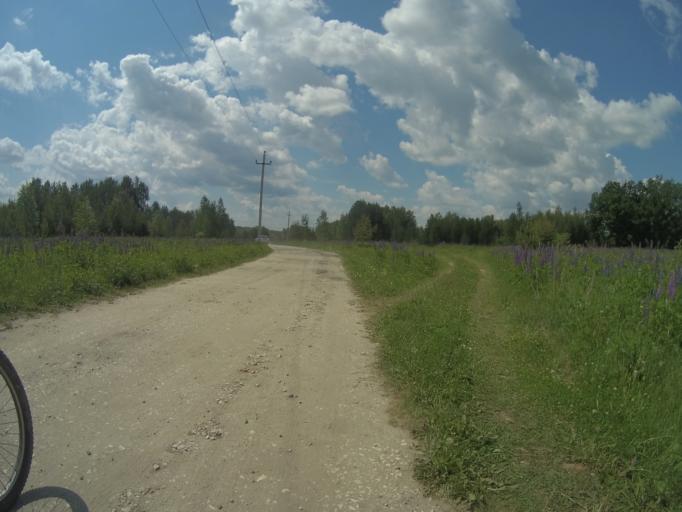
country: RU
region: Vladimir
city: Raduzhnyy
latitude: 55.9997
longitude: 40.2612
